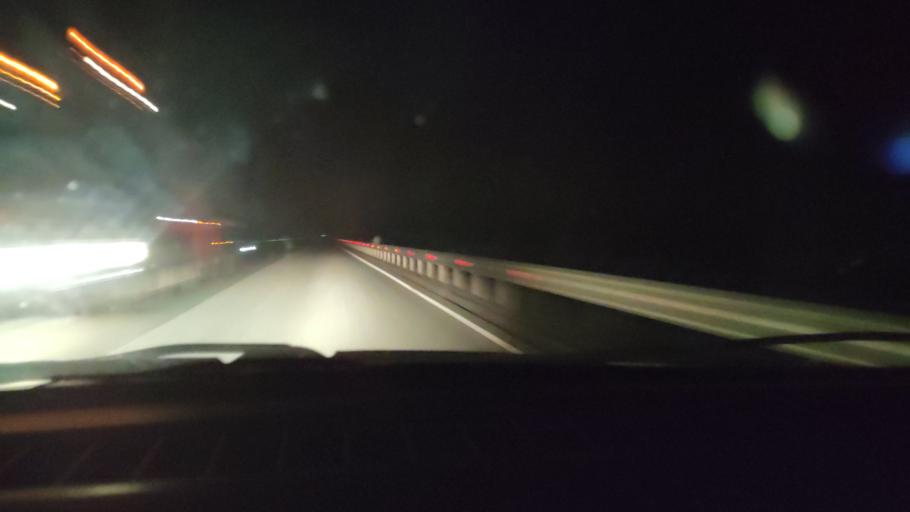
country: RU
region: Bashkortostan
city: Yermolayevo
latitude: 52.5156
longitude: 55.8311
